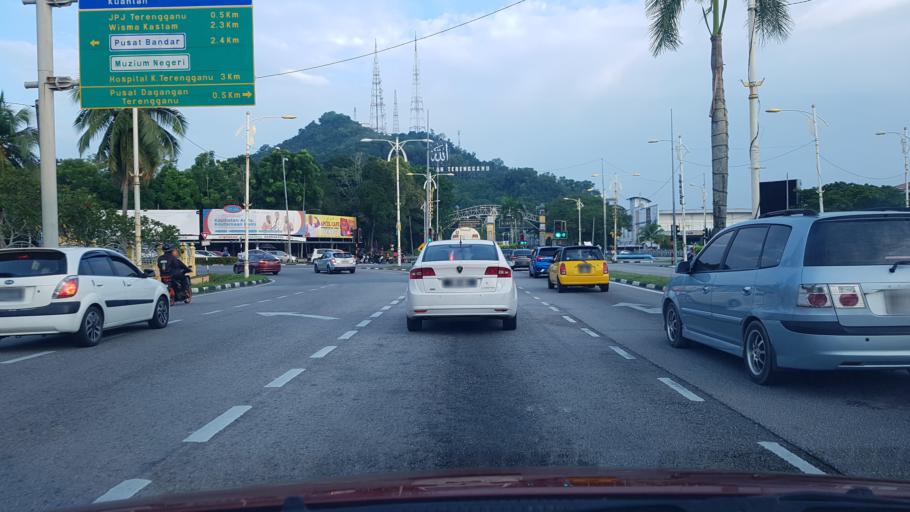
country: MY
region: Terengganu
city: Kuala Terengganu
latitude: 5.3141
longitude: 103.1306
